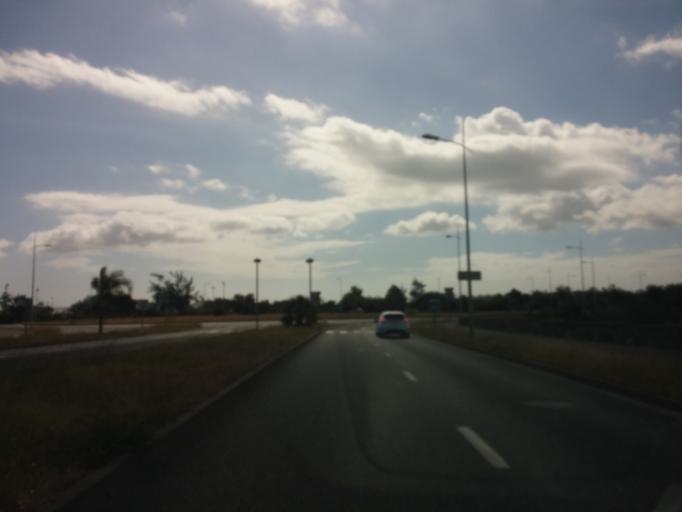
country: RE
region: Reunion
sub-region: Reunion
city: Le Port
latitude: -20.9538
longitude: 55.2945
